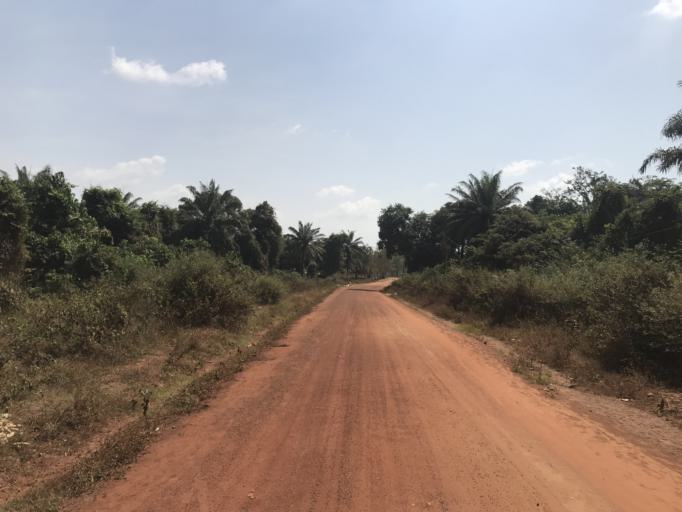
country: NG
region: Osun
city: Ifon
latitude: 7.8749
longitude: 4.4787
